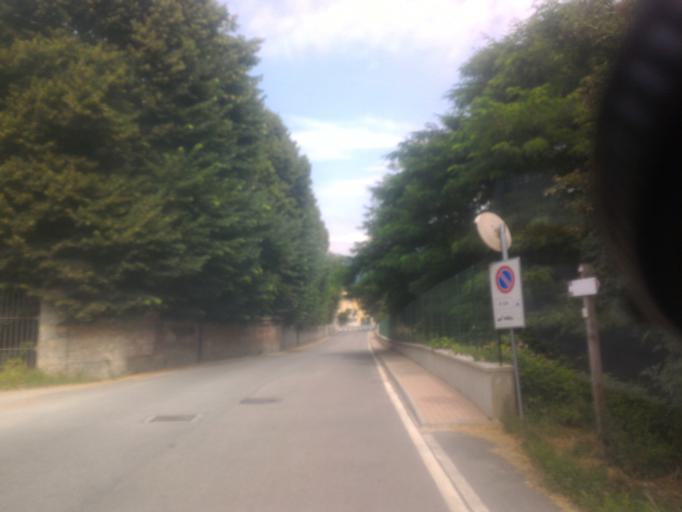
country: IT
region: Piedmont
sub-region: Provincia di Torino
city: San Secondo di Pinerolo
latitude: 44.8736
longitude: 7.3109
